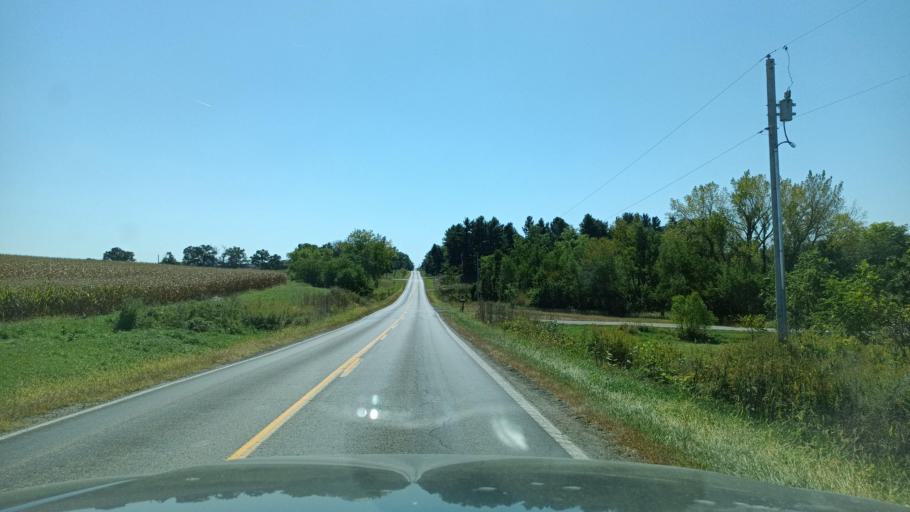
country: US
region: Illinois
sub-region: McLean County
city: Danvers
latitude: 40.6019
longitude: -89.2029
